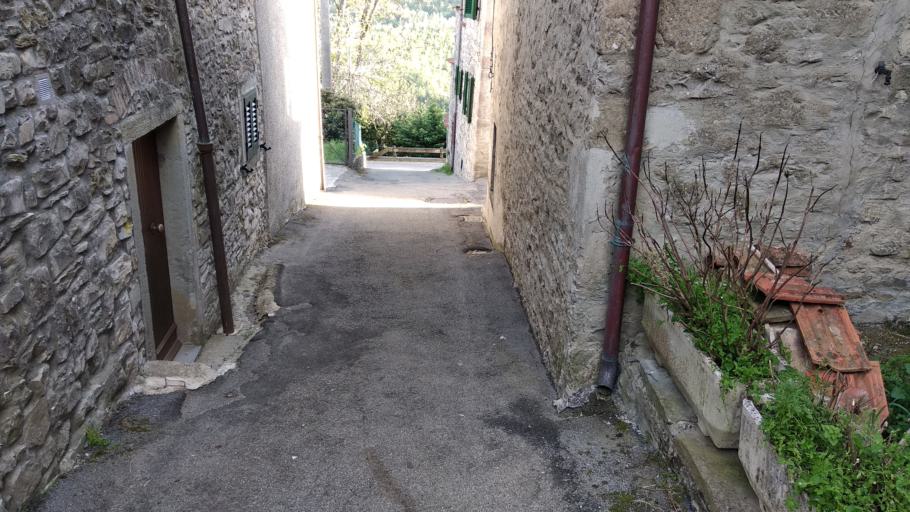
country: IT
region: Tuscany
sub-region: Province of Arezzo
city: Chiusi della Verna
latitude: 43.7496
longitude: 11.9346
